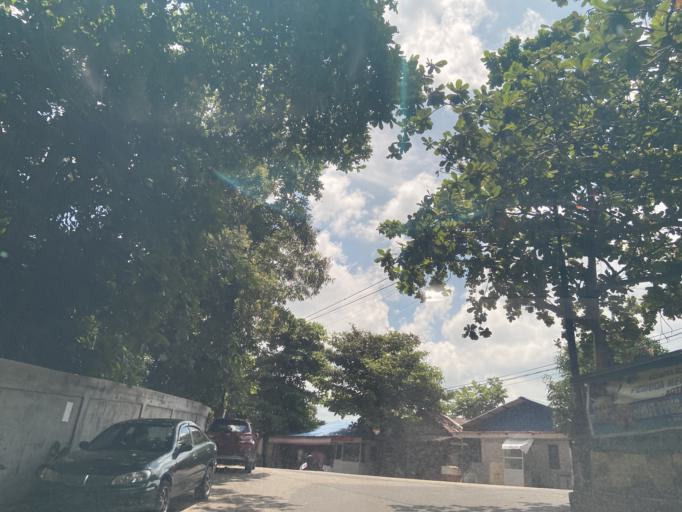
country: SG
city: Singapore
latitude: 1.1556
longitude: 104.0137
